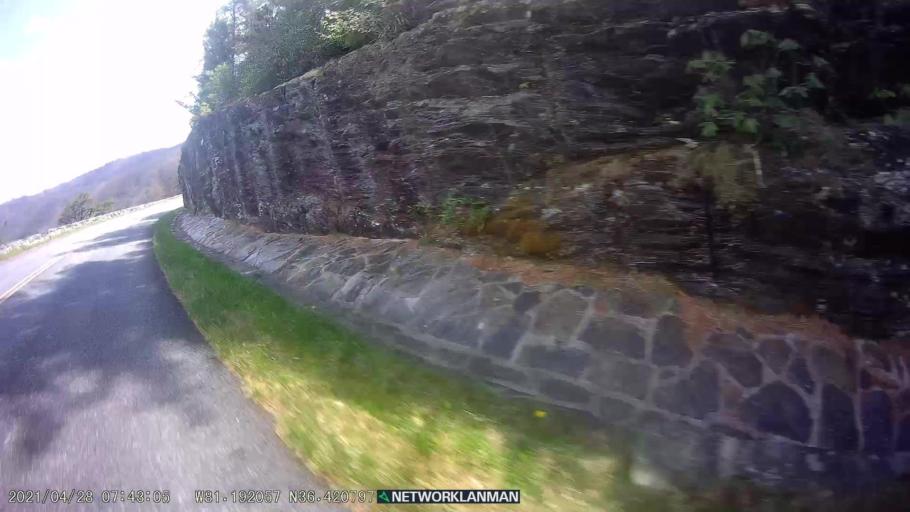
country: US
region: North Carolina
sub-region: Alleghany County
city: Sparta
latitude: 36.4232
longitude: -81.1928
